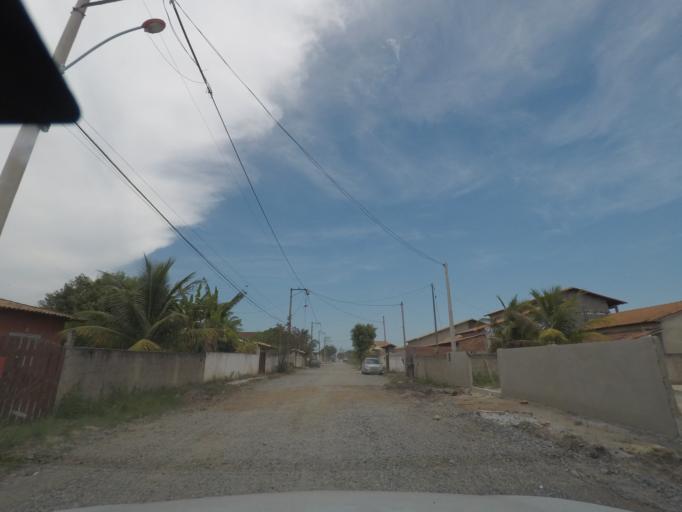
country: BR
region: Rio de Janeiro
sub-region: Marica
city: Marica
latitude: -22.9606
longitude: -42.9505
